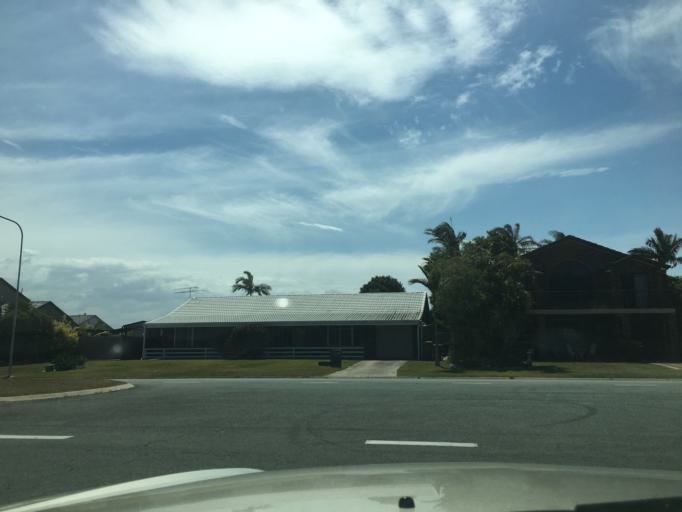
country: AU
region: Queensland
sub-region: Moreton Bay
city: Bongaree
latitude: -27.0827
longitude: 153.1358
